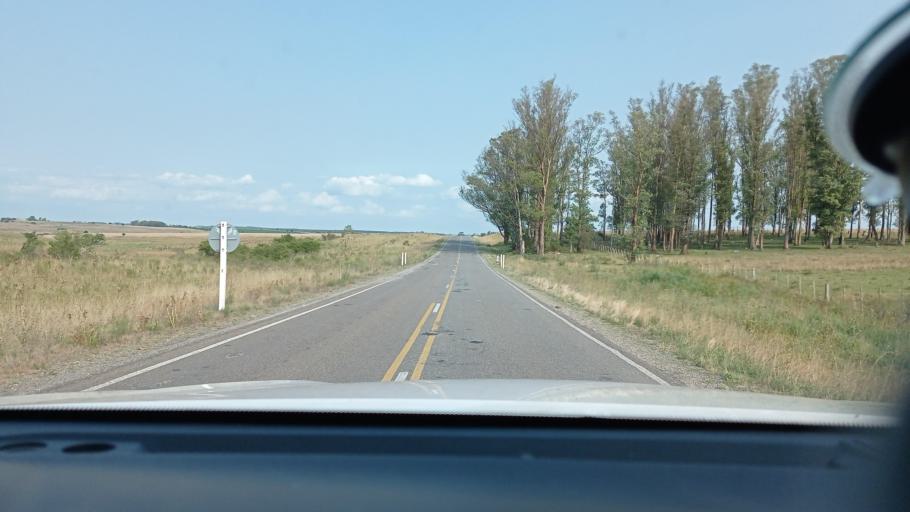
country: UY
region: Florida
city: Florida
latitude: -34.1728
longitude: -56.0868
